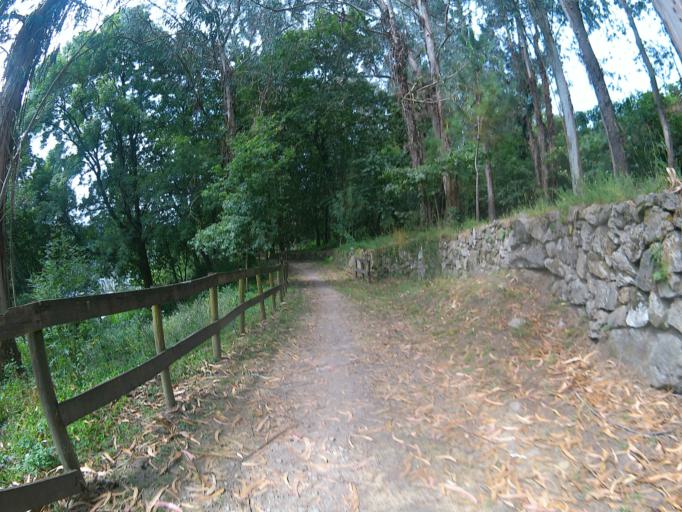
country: PT
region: Viana do Castelo
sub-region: Ponte de Lima
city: Ponte de Lima
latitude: 41.7781
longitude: -8.5547
